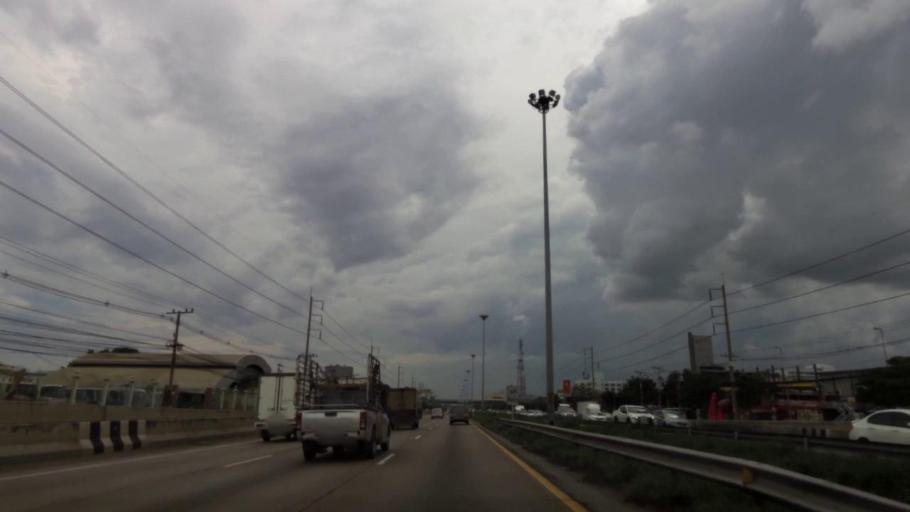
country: TH
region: Pathum Thani
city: Khlong Luang
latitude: 14.1372
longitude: 100.6185
